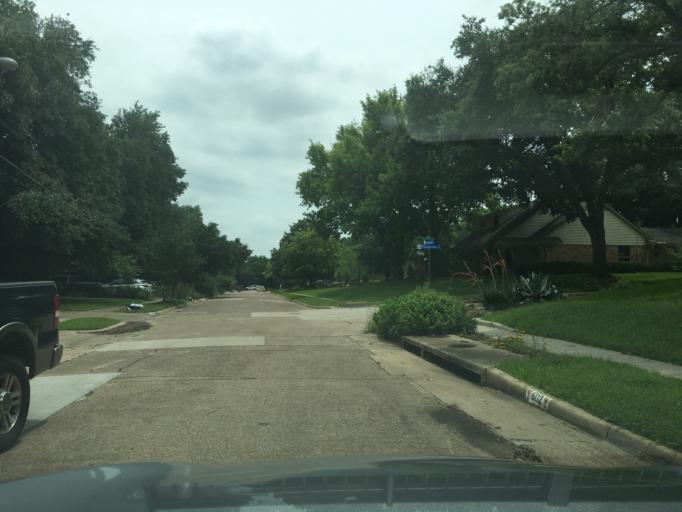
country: US
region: Texas
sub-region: Dallas County
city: Richardson
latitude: 32.9462
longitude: -96.7555
